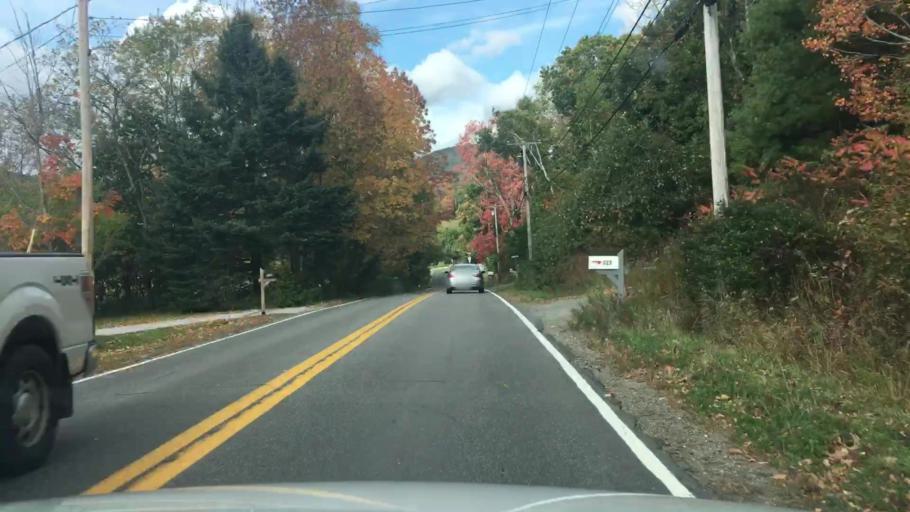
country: US
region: Maine
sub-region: Knox County
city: Camden
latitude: 44.2095
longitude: -69.0915
